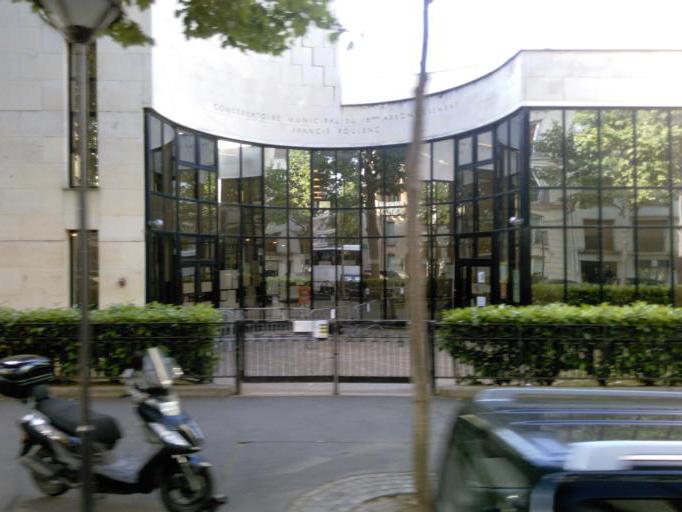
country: FR
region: Ile-de-France
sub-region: Departement des Hauts-de-Seine
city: Boulogne-Billancourt
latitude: 48.8521
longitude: 2.2748
